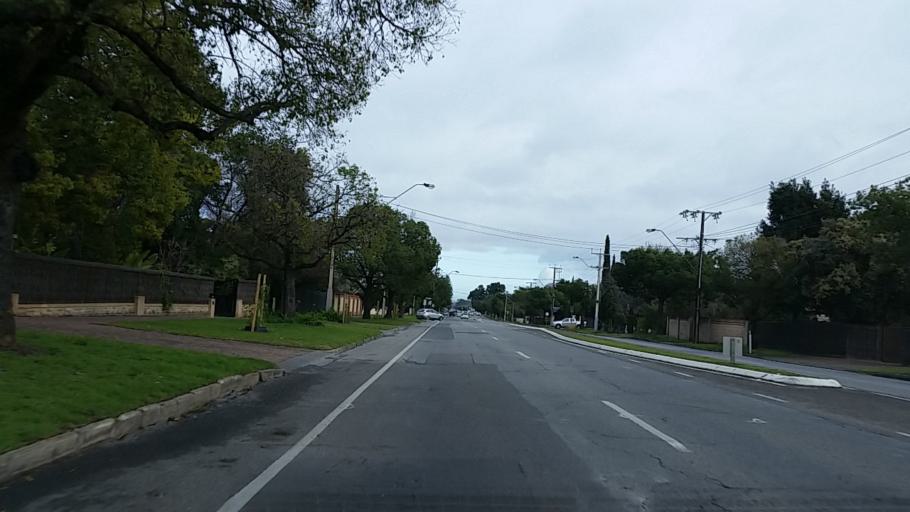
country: AU
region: South Australia
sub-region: Burnside
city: Tusmore
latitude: -34.9389
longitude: 138.6491
